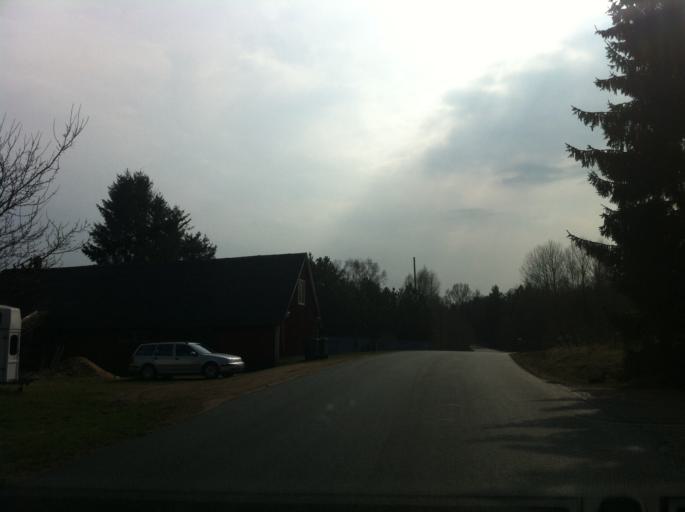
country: SE
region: Skane
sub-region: Perstorps Kommun
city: Perstorp
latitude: 56.0898
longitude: 13.4028
